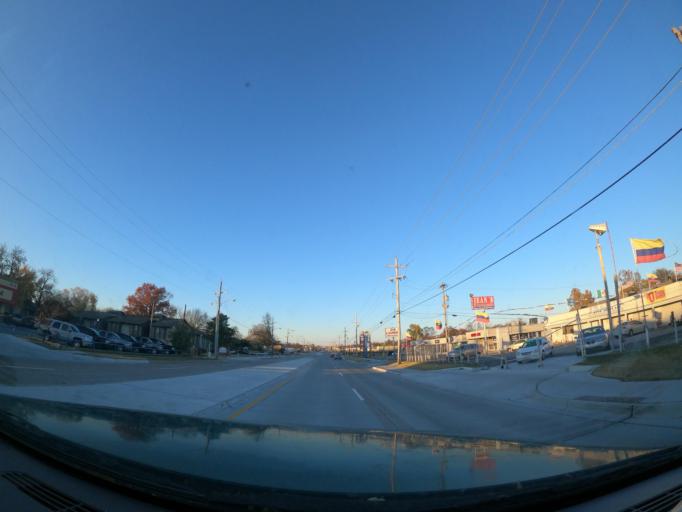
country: US
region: Oklahoma
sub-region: Tulsa County
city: Tulsa
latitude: 36.1377
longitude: -95.8866
